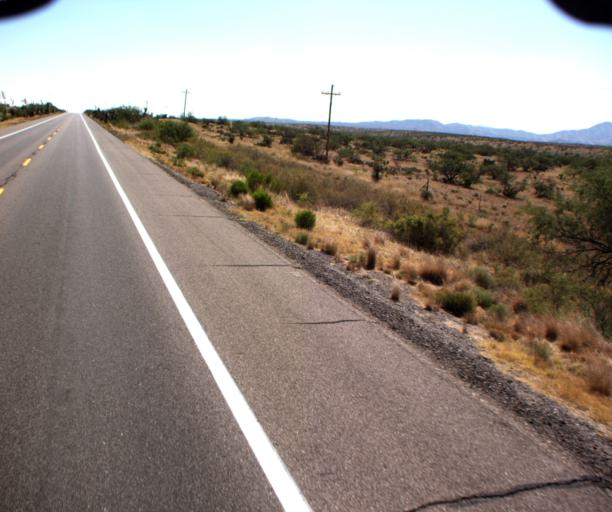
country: US
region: Arizona
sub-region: Pima County
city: Catalina
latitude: 32.5873
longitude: -110.9005
